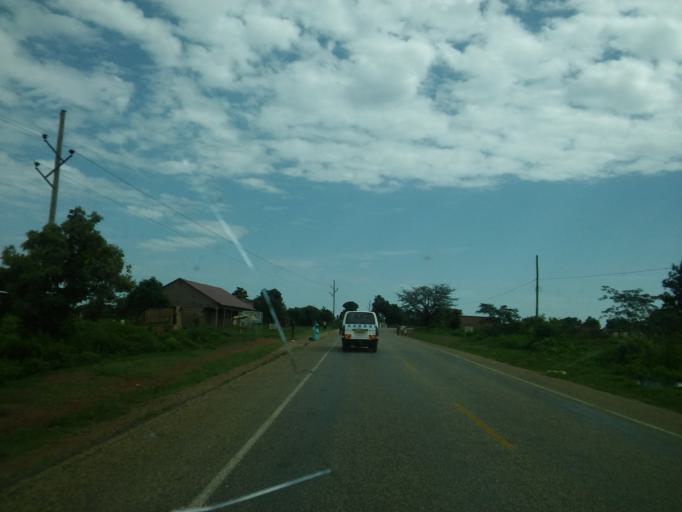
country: UG
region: Eastern Region
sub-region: Bukedea District
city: Bukedea
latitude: 1.2507
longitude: 34.0915
